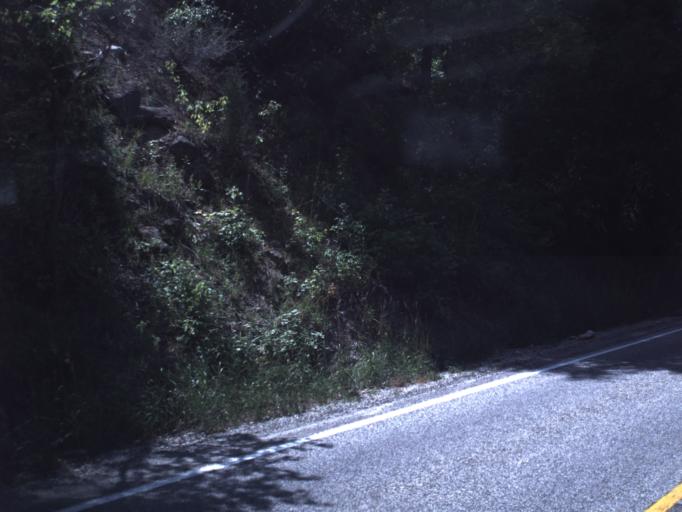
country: US
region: Utah
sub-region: Cache County
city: North Logan
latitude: 41.8139
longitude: -111.6203
